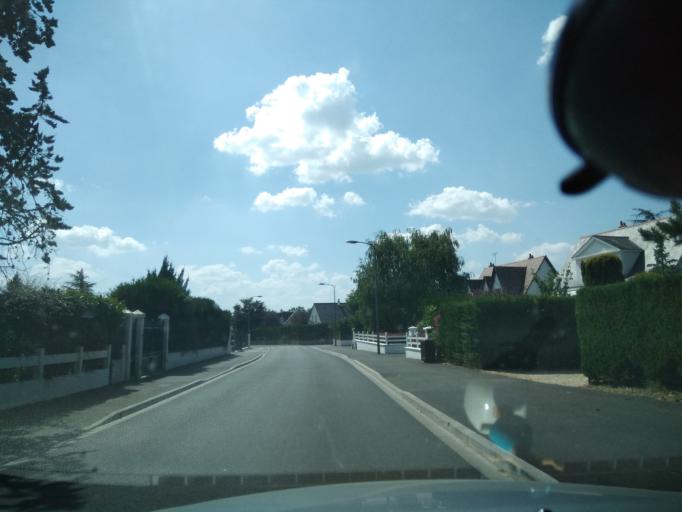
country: FR
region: Centre
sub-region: Departement d'Indre-et-Loire
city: Chambray-les-Tours
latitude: 47.3472
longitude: 0.6884
